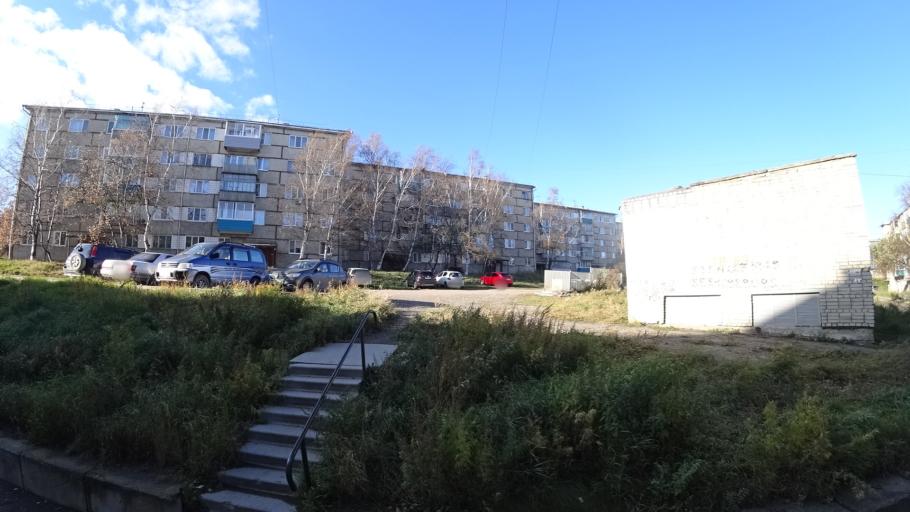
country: RU
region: Khabarovsk Krai
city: Amursk
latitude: 50.2406
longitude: 136.9058
